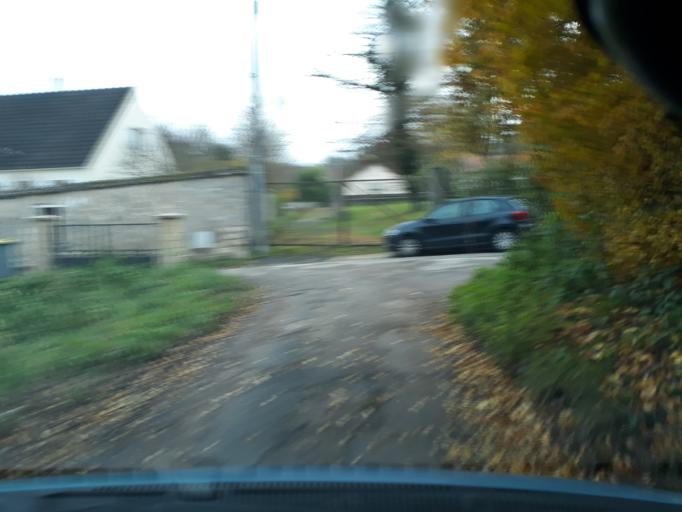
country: FR
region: Ile-de-France
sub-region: Departement de Seine-et-Marne
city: Veneux-les-Sablons
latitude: 48.3803
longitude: 2.7842
